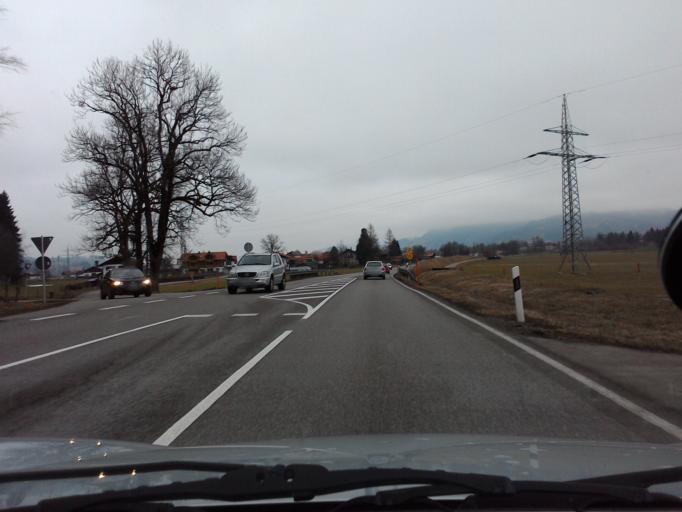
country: DE
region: Bavaria
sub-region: Swabia
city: Sonthofen
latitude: 47.5000
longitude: 10.2663
